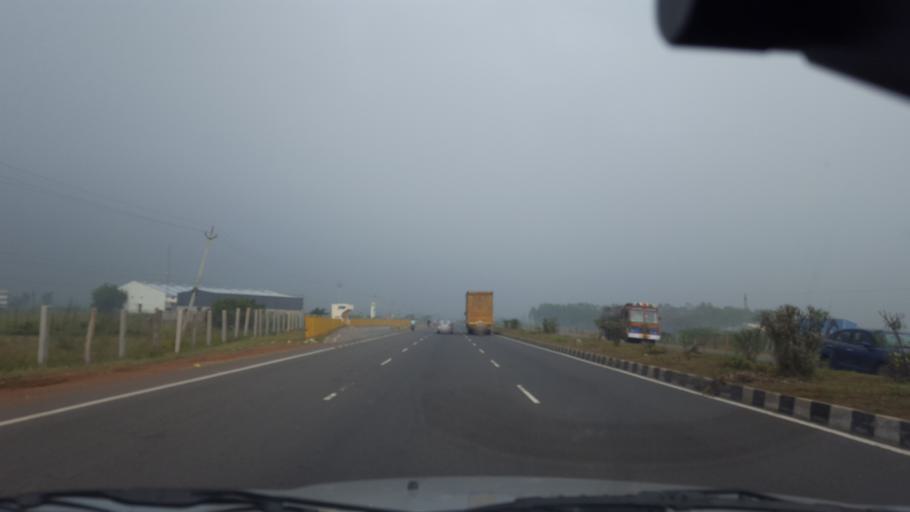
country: IN
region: Andhra Pradesh
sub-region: Prakasam
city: Ongole
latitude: 15.5761
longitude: 80.0432
